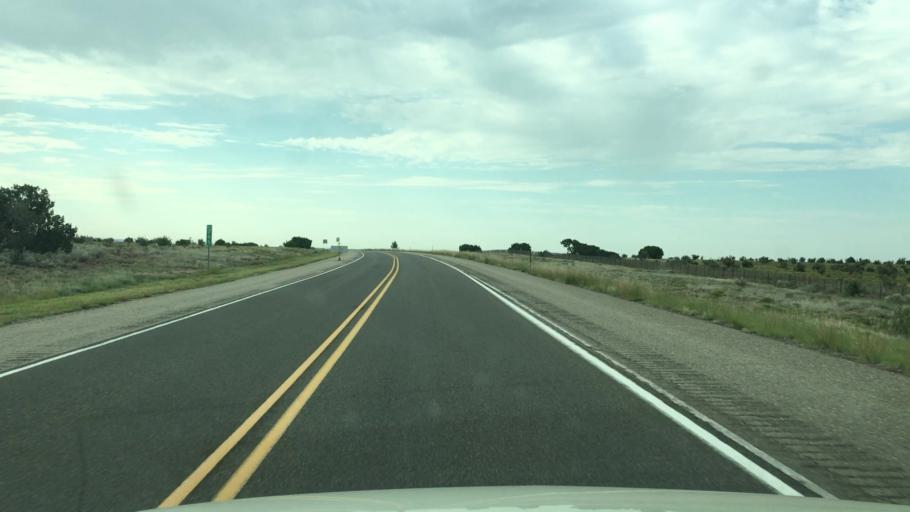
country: US
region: New Mexico
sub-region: Santa Fe County
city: Eldorado at Santa Fe
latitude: 35.2221
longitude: -105.8011
